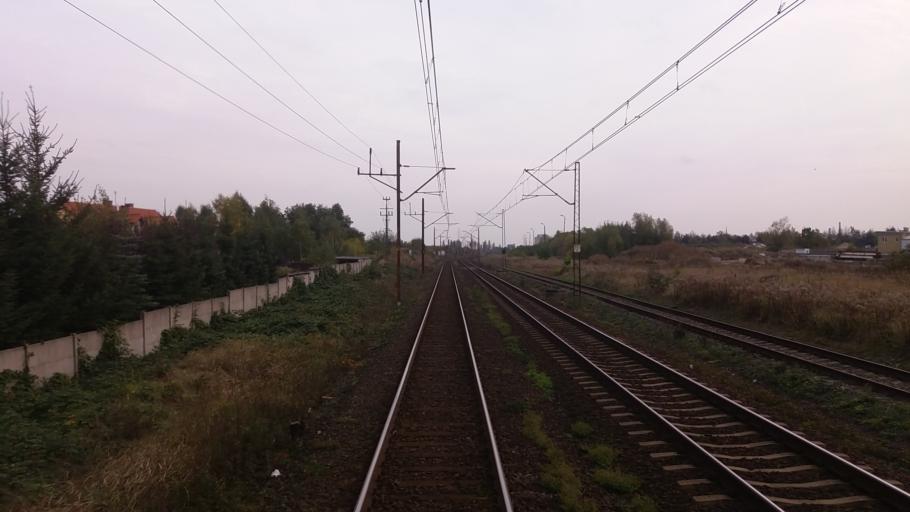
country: PL
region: West Pomeranian Voivodeship
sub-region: Powiat stargardzki
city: Stargard Szczecinski
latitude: 53.3542
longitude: 15.0028
